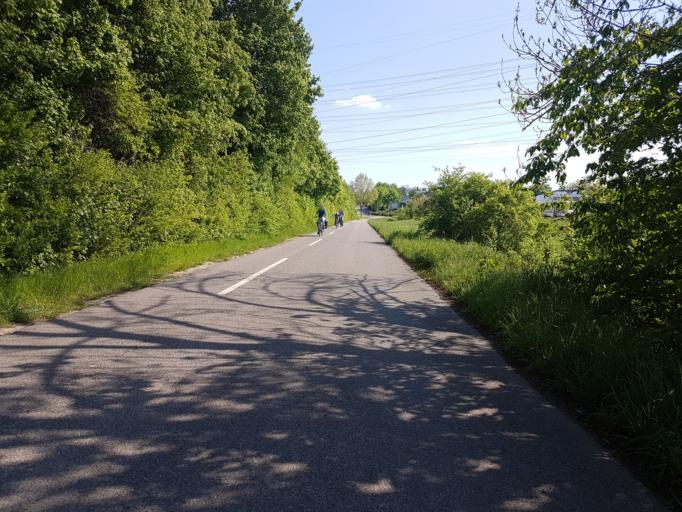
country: DE
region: Baden-Wuerttemberg
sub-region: Regierungsbezirk Stuttgart
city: Asperg
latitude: 48.9302
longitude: 9.1468
